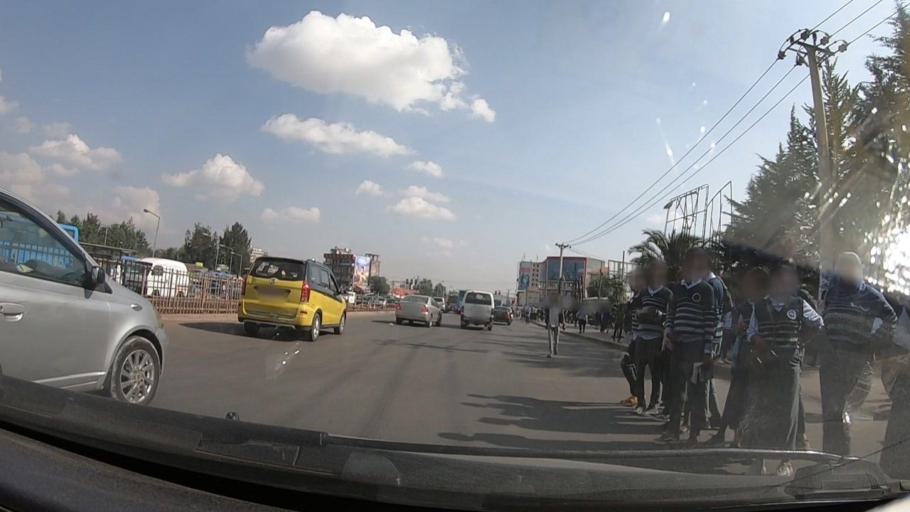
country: ET
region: Adis Abeba
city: Addis Ababa
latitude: 8.9836
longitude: 38.6963
